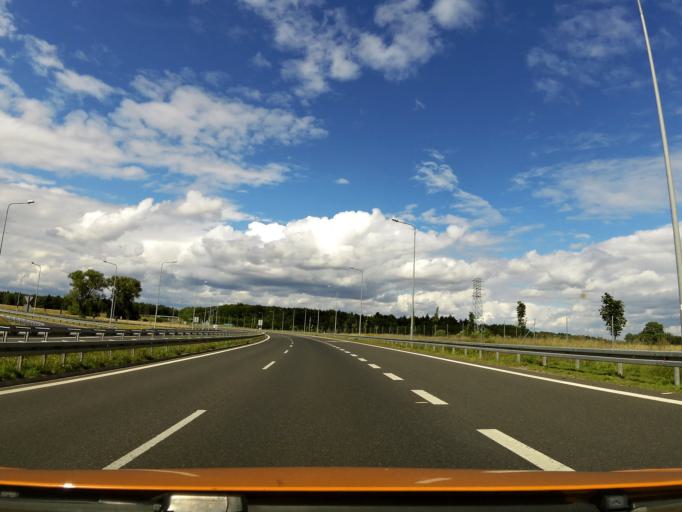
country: PL
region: West Pomeranian Voivodeship
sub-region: Powiat goleniowski
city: Nowogard
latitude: 53.6560
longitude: 15.0782
